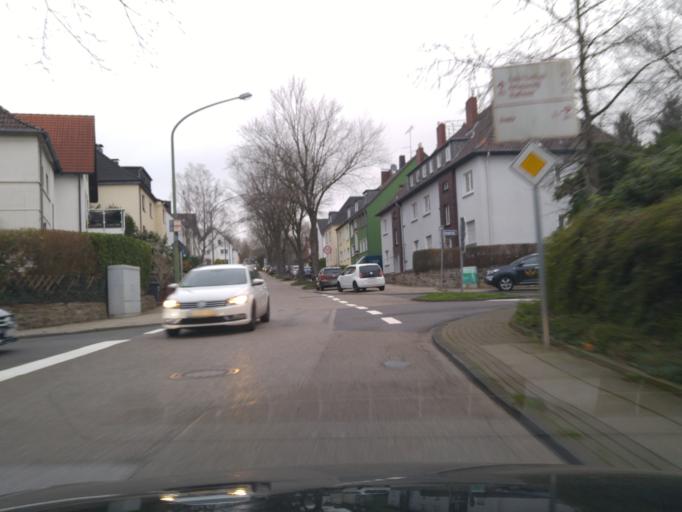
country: DE
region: North Rhine-Westphalia
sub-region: Regierungsbezirk Dusseldorf
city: Velbert
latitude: 51.4034
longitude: 7.0637
